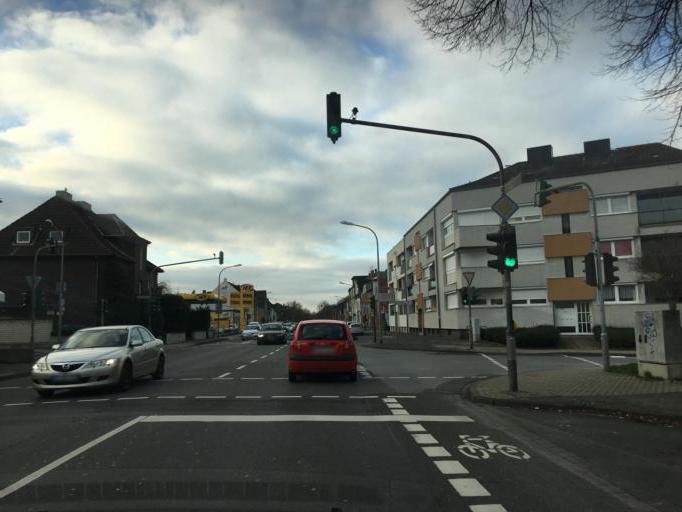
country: DE
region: North Rhine-Westphalia
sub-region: Regierungsbezirk Koln
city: Dueren
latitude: 50.7978
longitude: 6.4538
